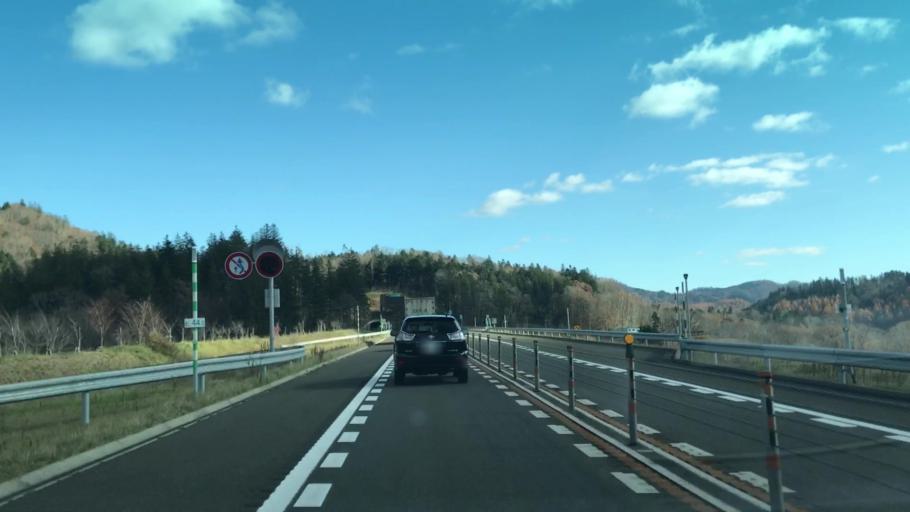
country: JP
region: Hokkaido
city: Iwamizawa
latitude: 42.9322
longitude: 142.0553
